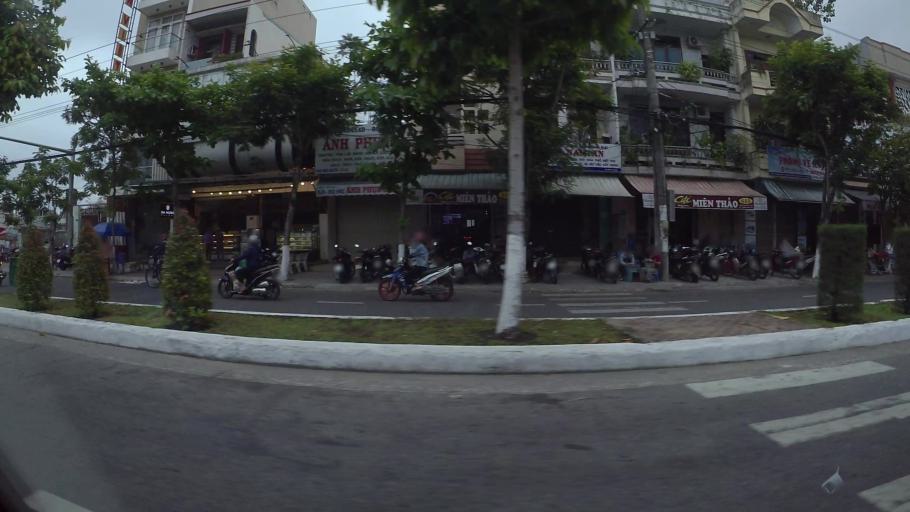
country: VN
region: Da Nang
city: Da Nang
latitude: 16.0774
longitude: 108.2318
